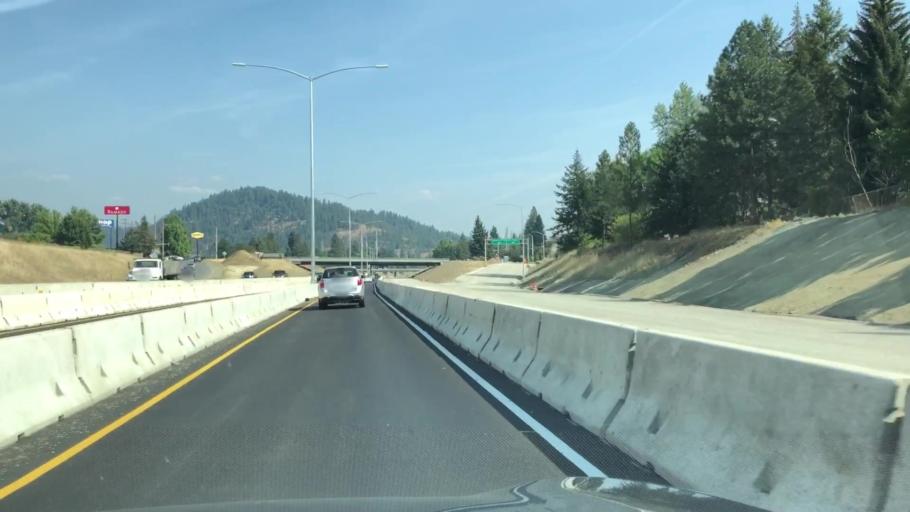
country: US
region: Idaho
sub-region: Kootenai County
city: Coeur d'Alene
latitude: 47.6981
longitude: -116.7855
